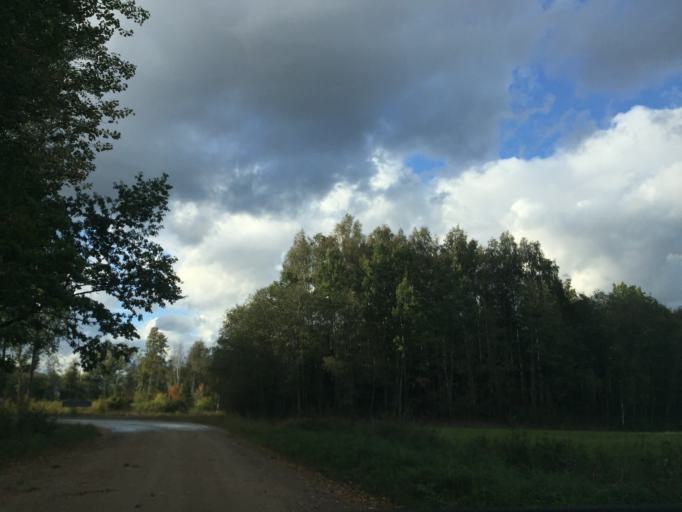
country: LV
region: Ligatne
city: Ligatne
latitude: 57.1385
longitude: 25.0832
